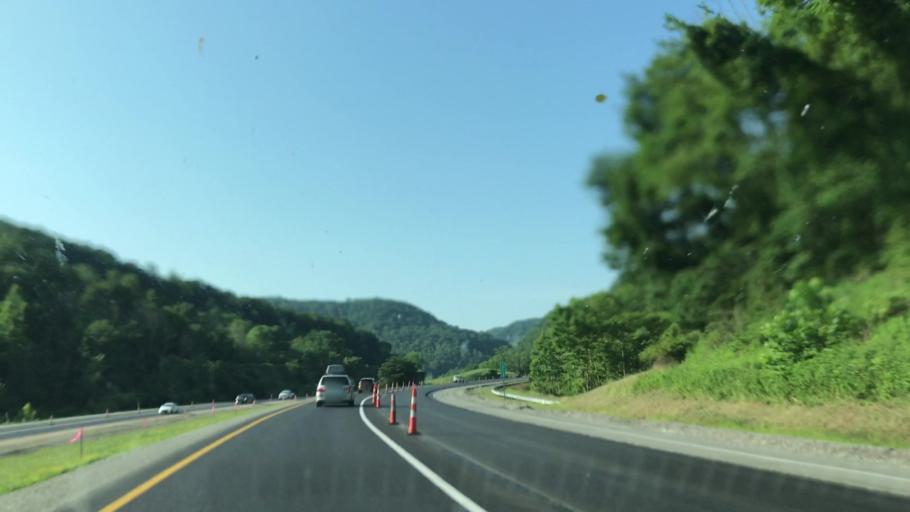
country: US
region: West Virginia
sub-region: Braxton County
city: Sutton
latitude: 38.7539
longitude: -80.6776
